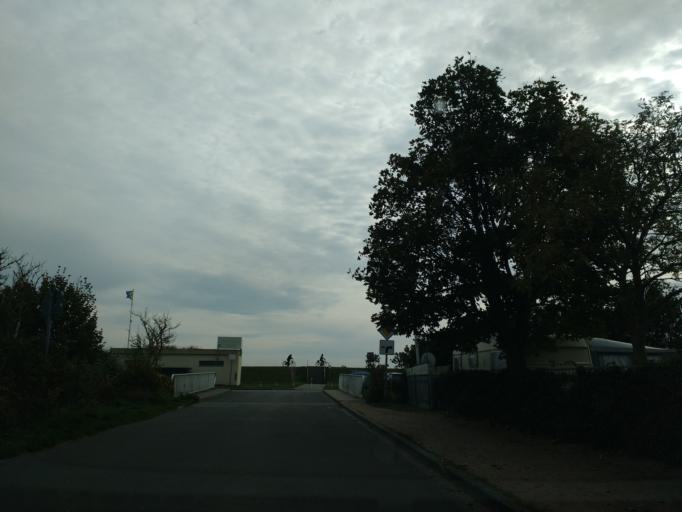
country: DE
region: Schleswig-Holstein
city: Gromitz
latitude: 54.1629
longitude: 11.0066
